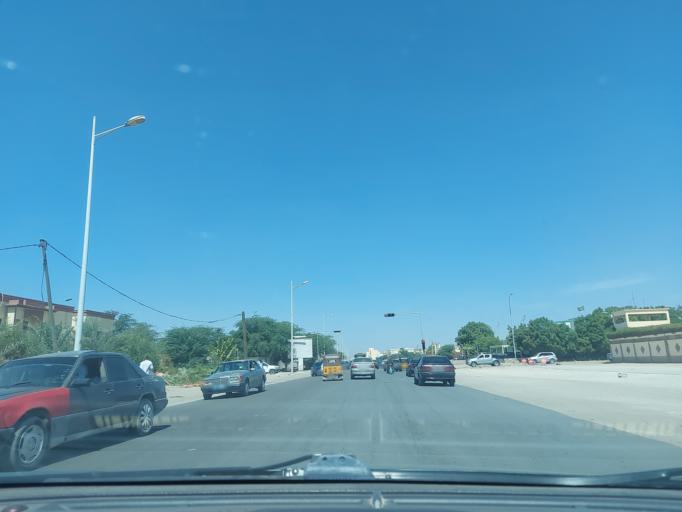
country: MR
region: Nouakchott
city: Nouakchott
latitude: 18.0799
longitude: -15.9682
